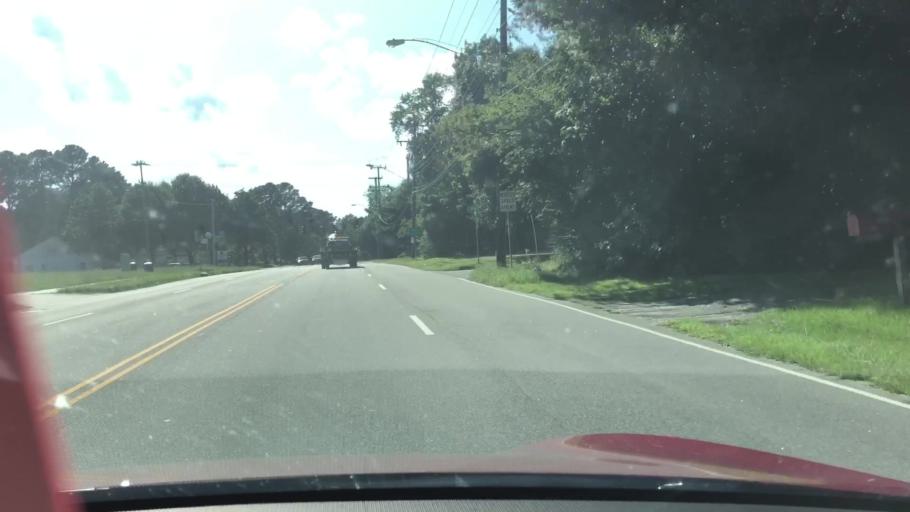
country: US
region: Virginia
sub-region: City of Virginia Beach
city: Virginia Beach
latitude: 36.8428
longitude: -76.0117
